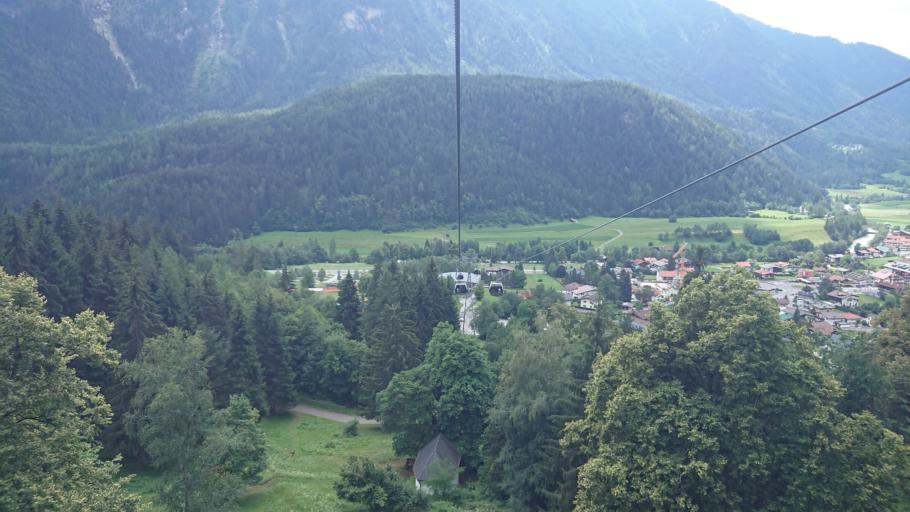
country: AT
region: Tyrol
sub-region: Politischer Bezirk Imst
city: Oetz
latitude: 47.2020
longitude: 10.9081
